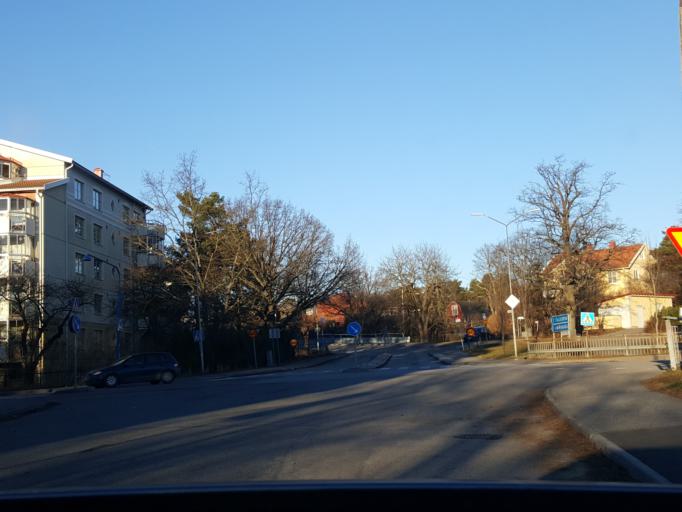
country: SE
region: Stockholm
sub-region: Nacka Kommun
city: Fisksatra
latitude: 59.3155
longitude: 18.2341
